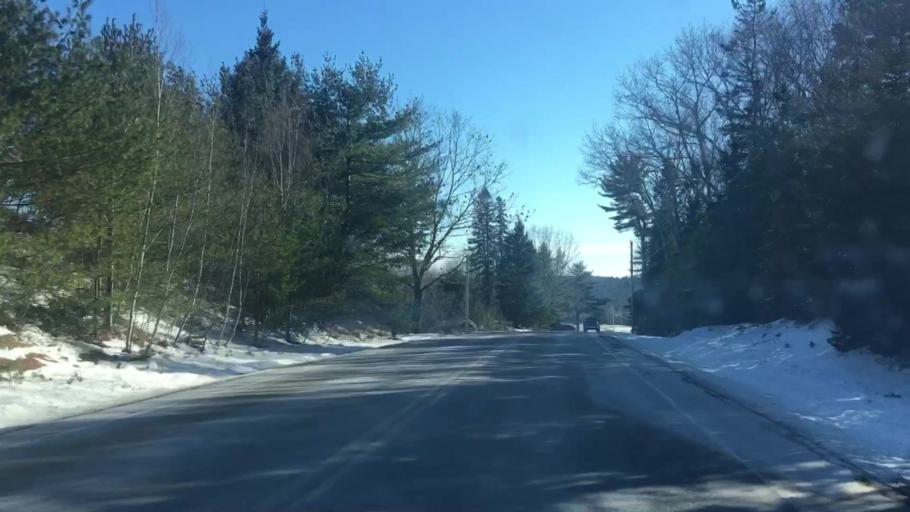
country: US
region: Maine
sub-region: Hancock County
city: Sedgwick
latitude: 44.3763
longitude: -68.6589
